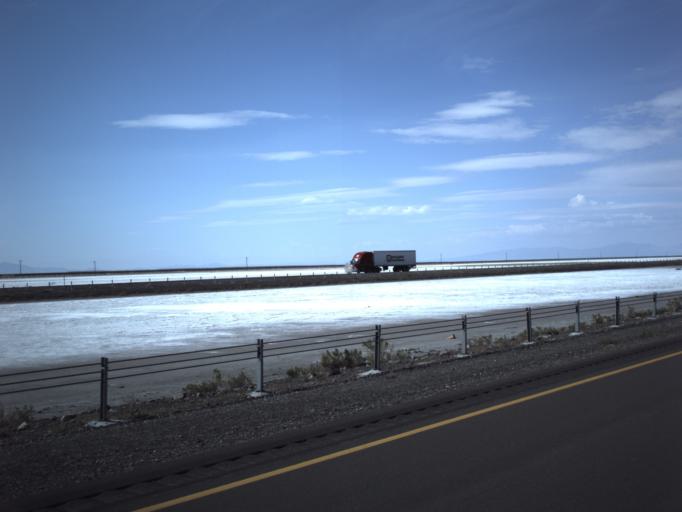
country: US
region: Utah
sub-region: Tooele County
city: Wendover
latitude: 40.7294
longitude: -113.3990
